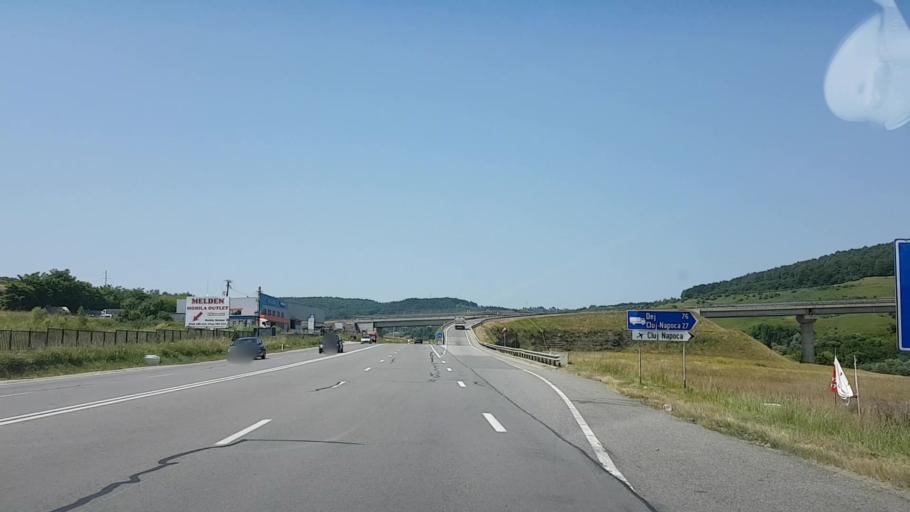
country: RO
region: Cluj
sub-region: Comuna Feleacu
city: Feleacu
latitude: 46.6867
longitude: 23.6324
